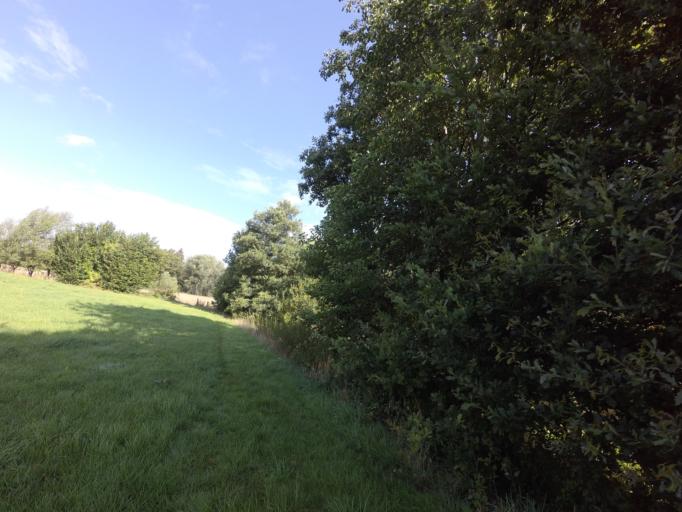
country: BE
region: Wallonia
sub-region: Province de Liege
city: Plombieres
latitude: 50.7482
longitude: 5.9458
